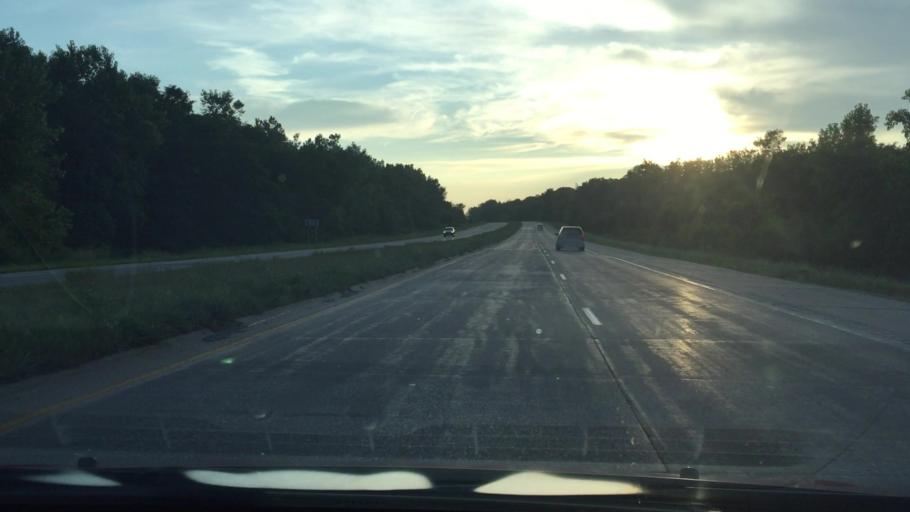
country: US
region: Iowa
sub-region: Muscatine County
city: Muscatine
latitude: 41.4524
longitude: -91.0464
